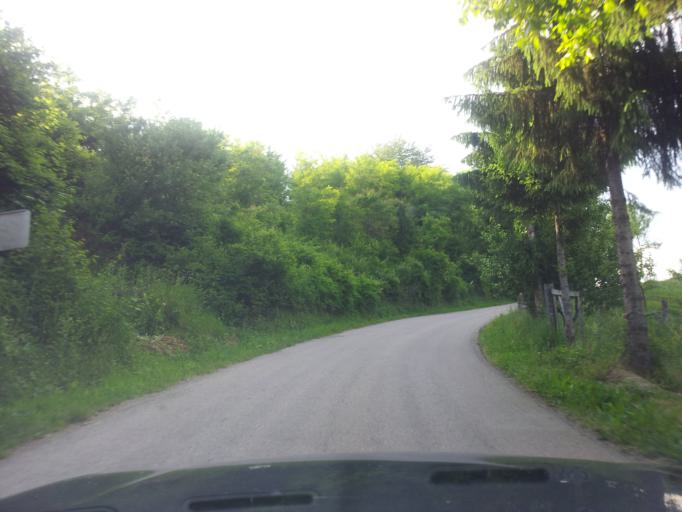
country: HR
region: Karlovacka
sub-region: Grad Karlovac
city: Karlovac
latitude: 45.4761
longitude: 15.4574
